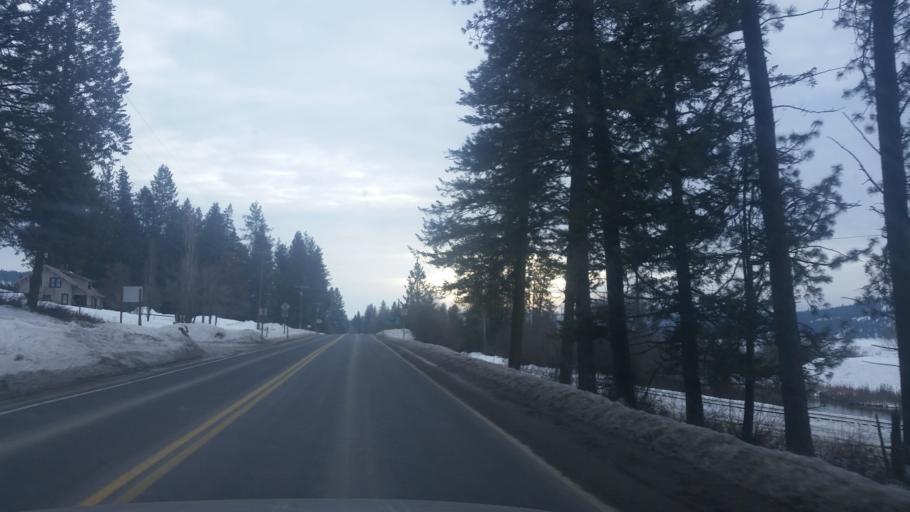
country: US
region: Washington
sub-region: Stevens County
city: Chewelah
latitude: 48.1662
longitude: -117.7228
